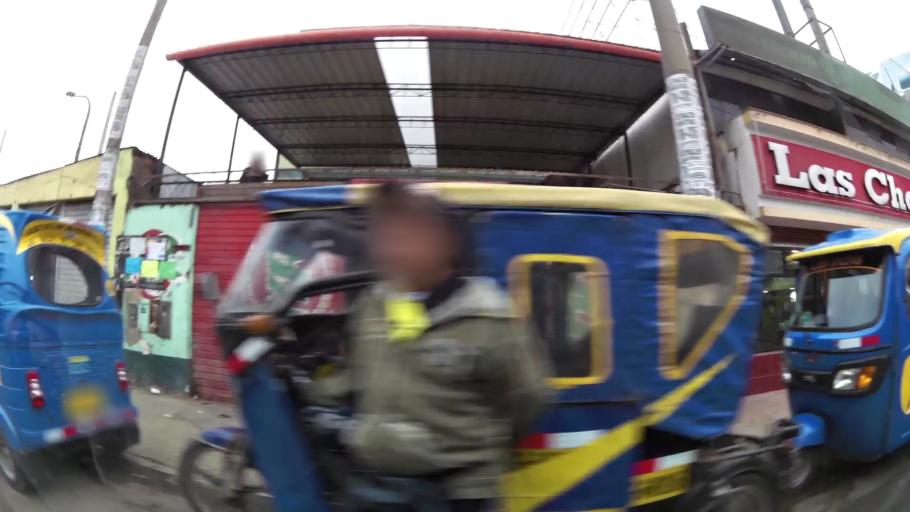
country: PE
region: Lima
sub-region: Lima
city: Urb. Santo Domingo
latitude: -11.9169
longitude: -77.0416
